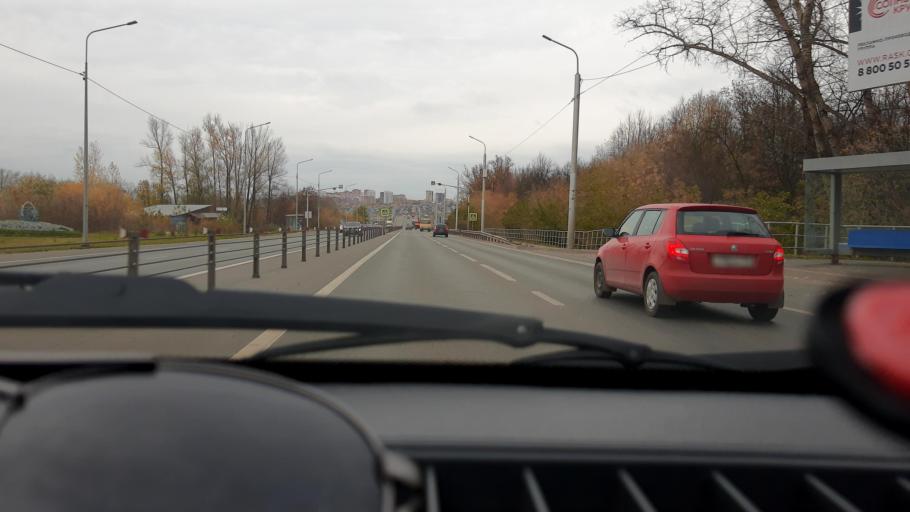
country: RU
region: Bashkortostan
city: Ufa
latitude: 54.7014
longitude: 55.9368
